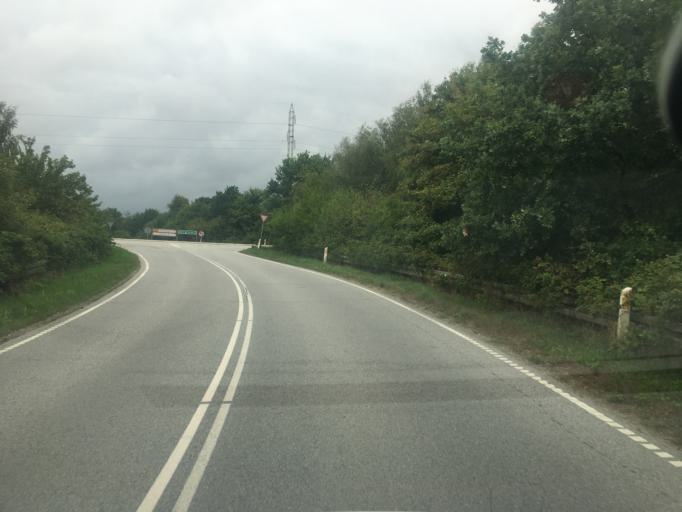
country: DK
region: South Denmark
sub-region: Haderslev Kommune
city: Vojens
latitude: 55.2475
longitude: 9.2909
